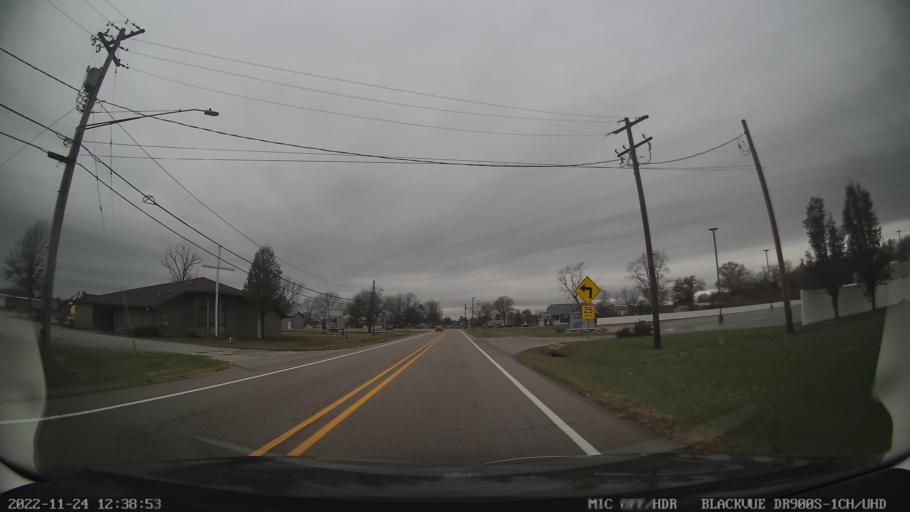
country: US
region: Illinois
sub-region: Macoupin County
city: Staunton
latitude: 39.0023
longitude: -89.7979
